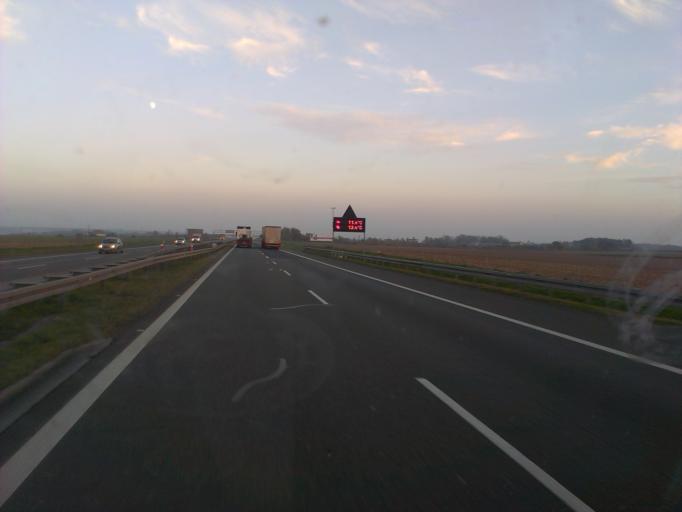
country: PL
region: Opole Voivodeship
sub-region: Powiat krapkowicki
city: Krapkowice
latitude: 50.5271
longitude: 17.9234
